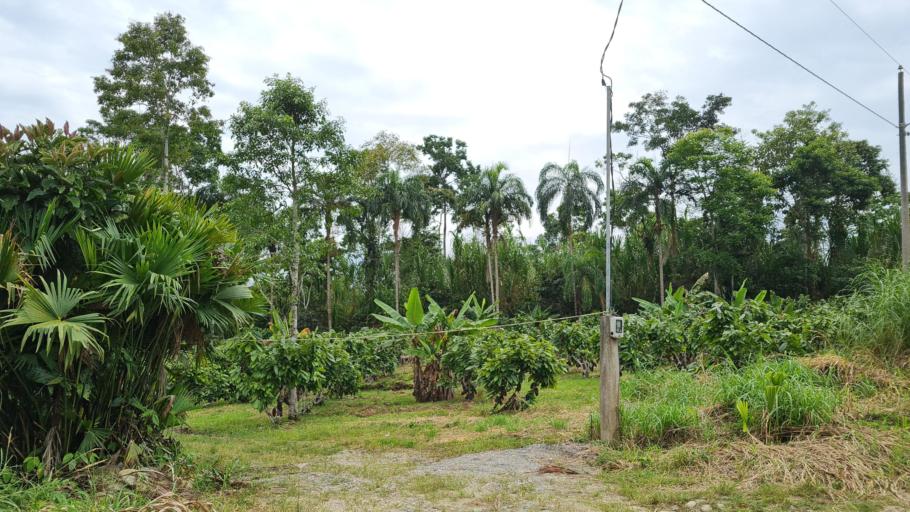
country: EC
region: Napo
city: Tena
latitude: -0.9979
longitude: -77.7543
